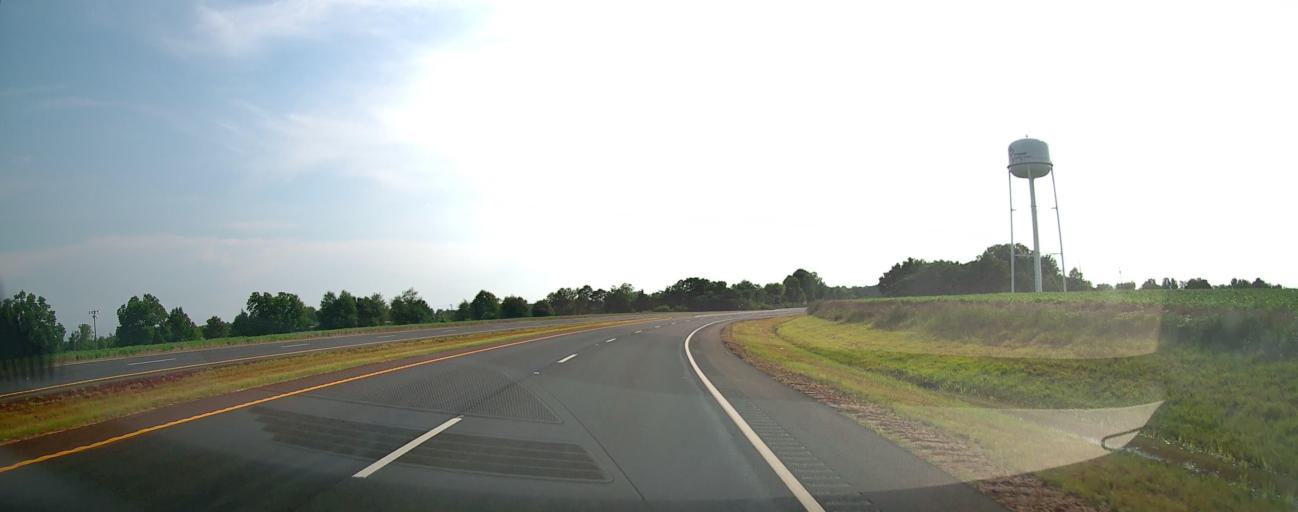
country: US
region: Georgia
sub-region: Peach County
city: Fort Valley
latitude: 32.5723
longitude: -83.9130
